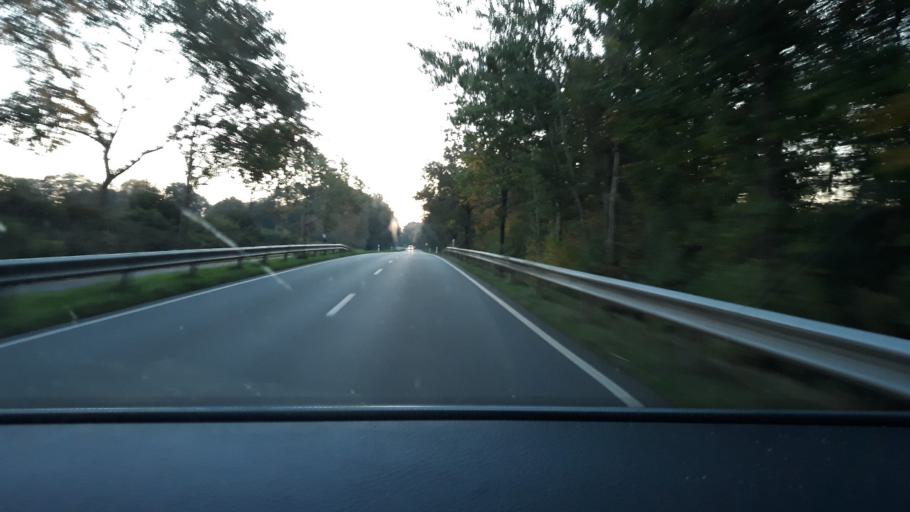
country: DE
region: Schleswig-Holstein
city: Dannewerk
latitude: 54.4789
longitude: 9.5204
